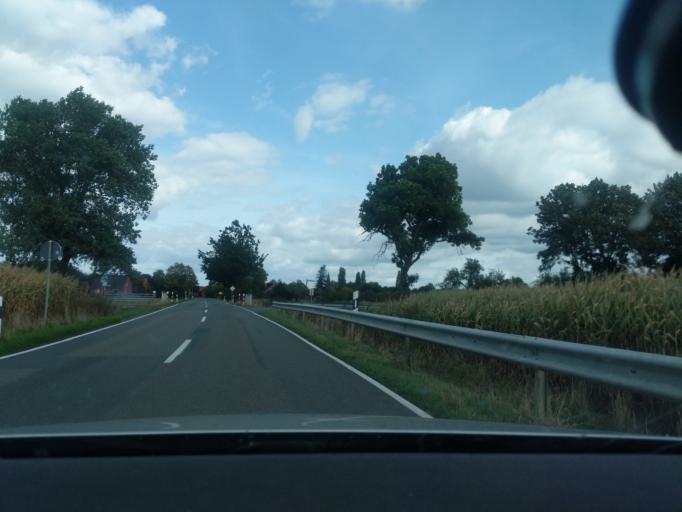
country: DE
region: Lower Saxony
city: Bucken
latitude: 52.7761
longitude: 9.1171
